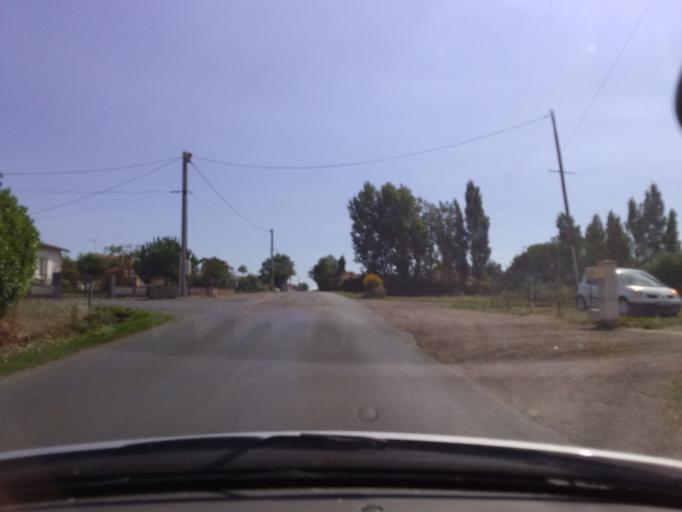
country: FR
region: Pays de la Loire
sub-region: Departement de la Vendee
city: Les Magnils-Reigniers
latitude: 46.4543
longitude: -1.2618
